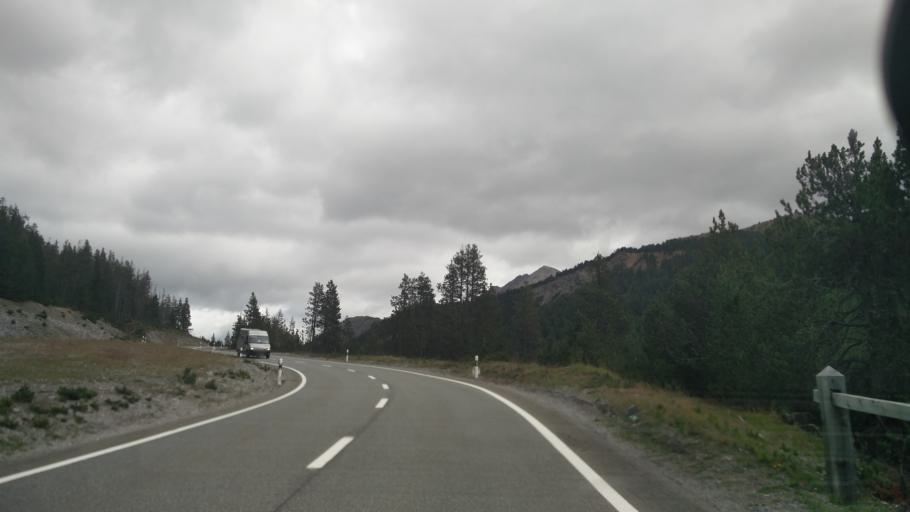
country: CH
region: Grisons
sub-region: Inn District
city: Scuol
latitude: 46.6576
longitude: 10.2434
